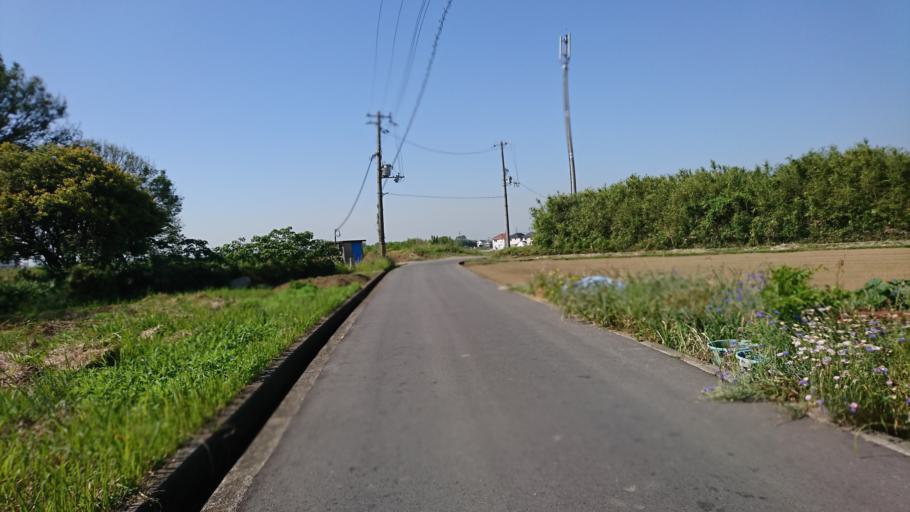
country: JP
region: Hyogo
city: Kakogawacho-honmachi
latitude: 34.7601
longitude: 134.8820
